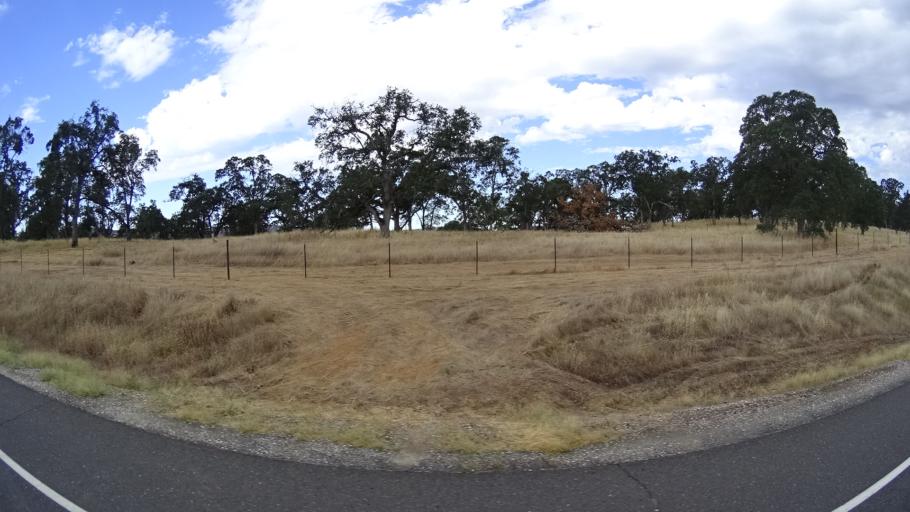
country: US
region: California
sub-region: Calaveras County
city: Copperopolis
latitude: 37.9475
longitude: -120.6514
